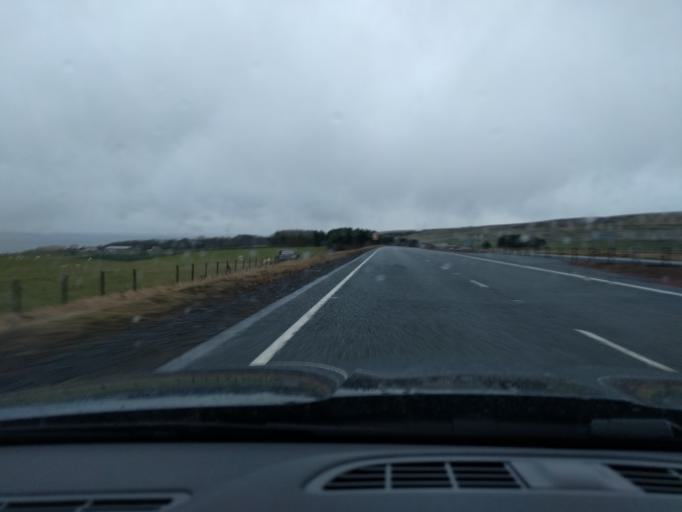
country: GB
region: England
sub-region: Northumberland
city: Berwick-Upon-Tweed
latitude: 55.8094
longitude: -2.0443
